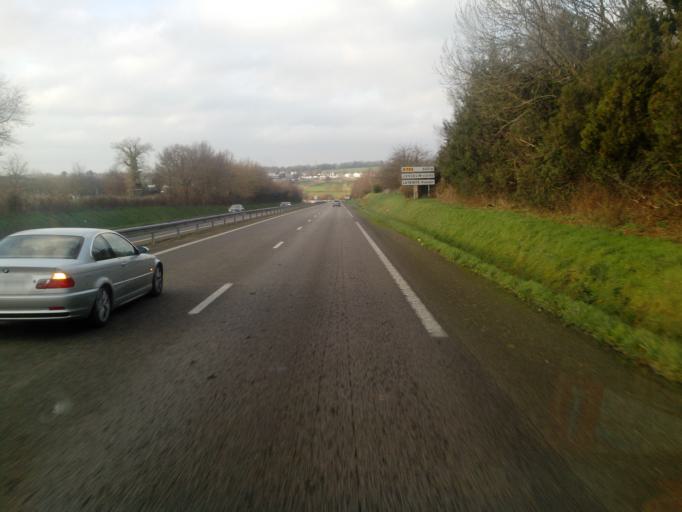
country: FR
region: Brittany
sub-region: Departement du Morbihan
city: Josselin
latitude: 47.9580
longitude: -2.5342
